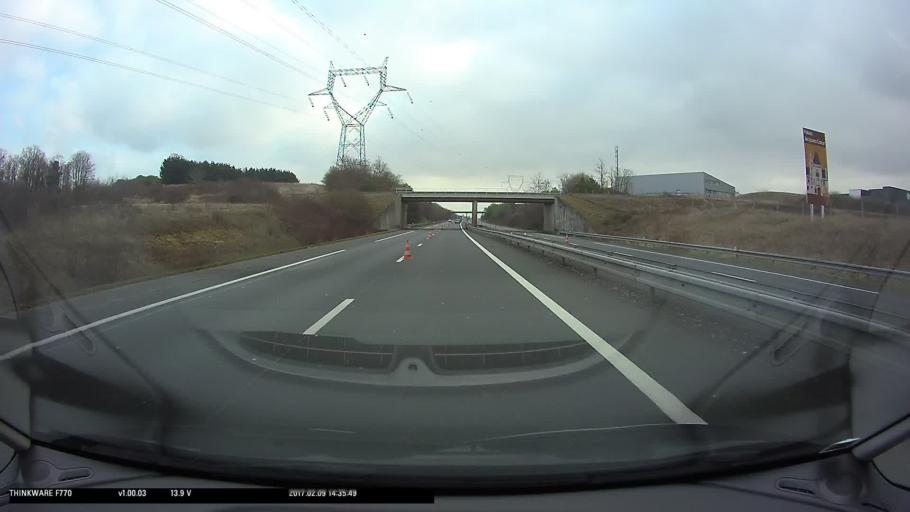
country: FR
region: Centre
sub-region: Departement du Cher
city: La Chapelle-Saint-Ursin
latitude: 47.0590
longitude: 2.3059
